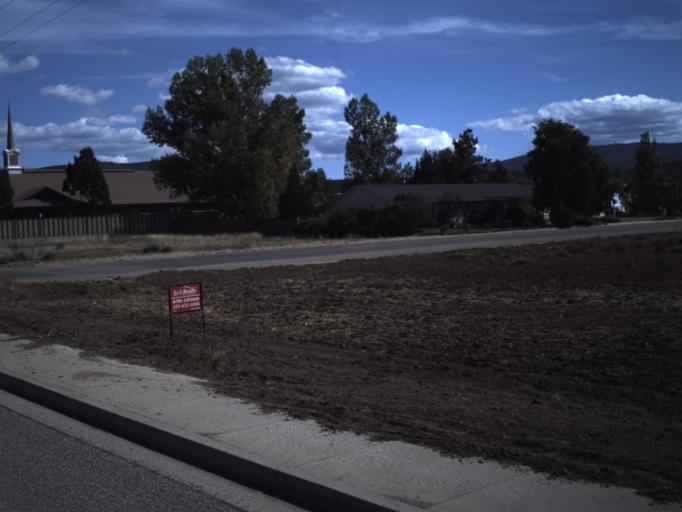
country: US
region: Utah
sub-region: Washington County
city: Enterprise
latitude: 37.5736
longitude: -113.7099
